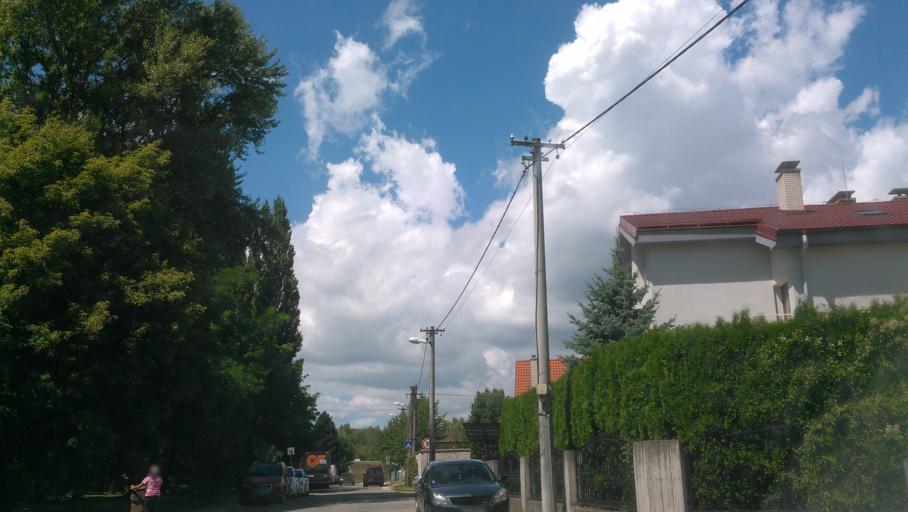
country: SK
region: Bratislavsky
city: Bratislava
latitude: 48.1249
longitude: 17.0917
